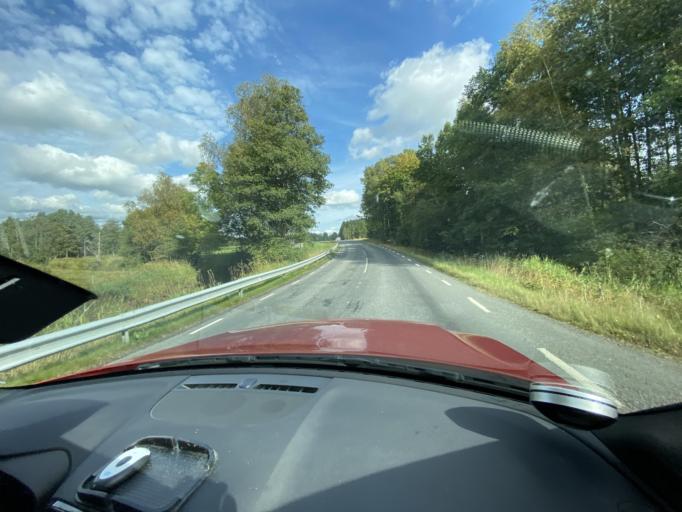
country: SE
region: Skane
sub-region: Hassleholms Kommun
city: Bjarnum
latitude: 56.3551
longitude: 13.7765
